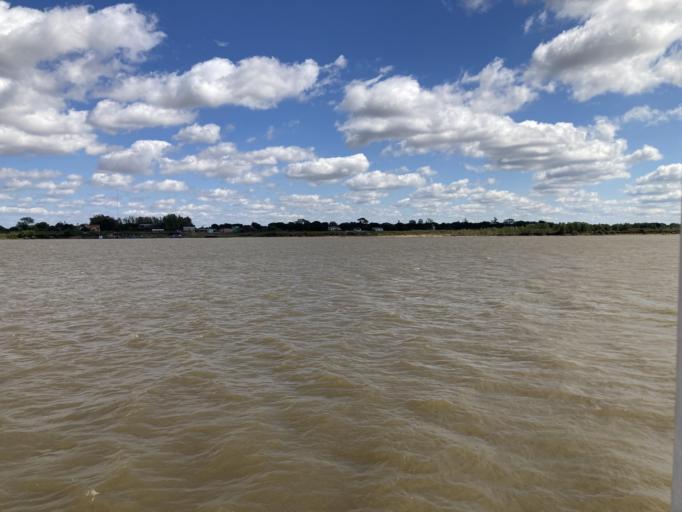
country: PY
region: Presidente Hayes
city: Nanawa
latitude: -25.2603
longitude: -57.6349
